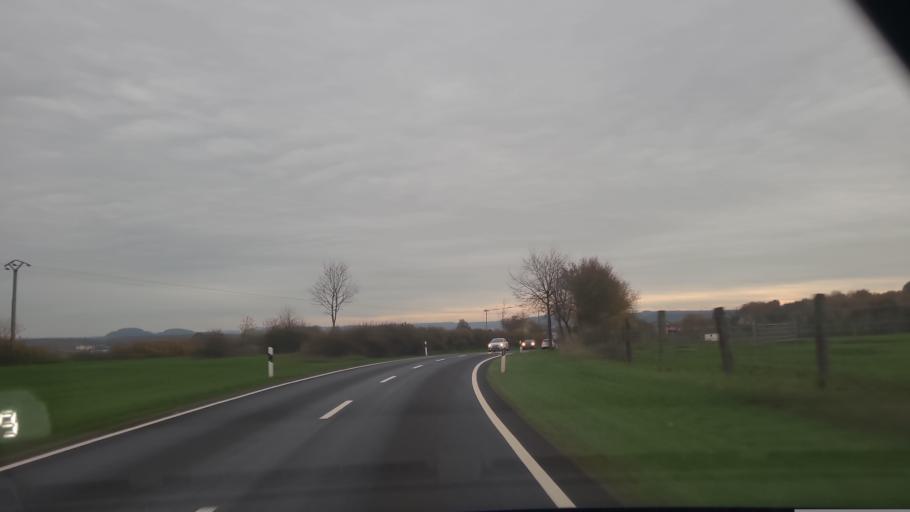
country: LU
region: Luxembourg
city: Hautcharage
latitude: 49.5857
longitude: 5.9110
